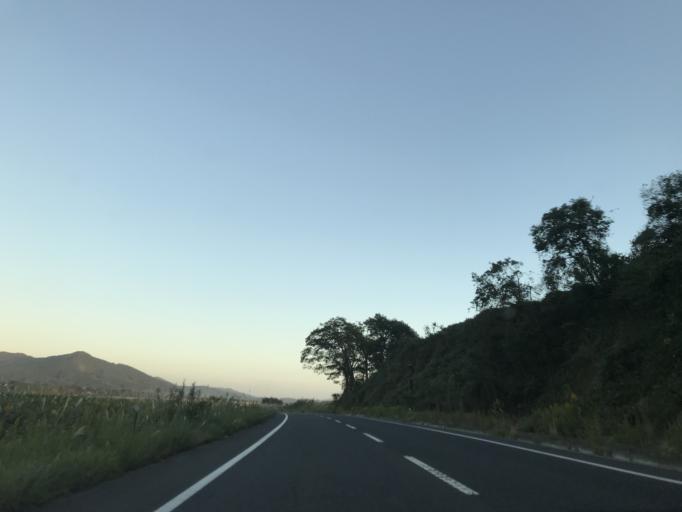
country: JP
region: Iwate
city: Ichinoseki
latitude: 38.9970
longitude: 141.1152
